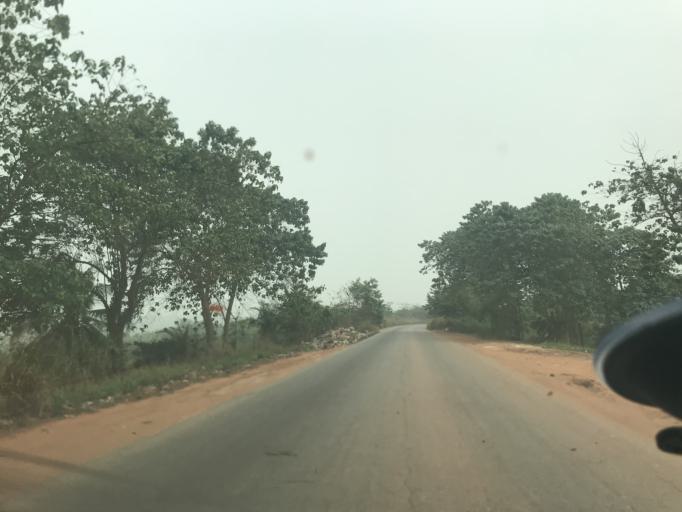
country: NG
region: Ogun
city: Ifo
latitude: 6.8848
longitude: 3.1254
